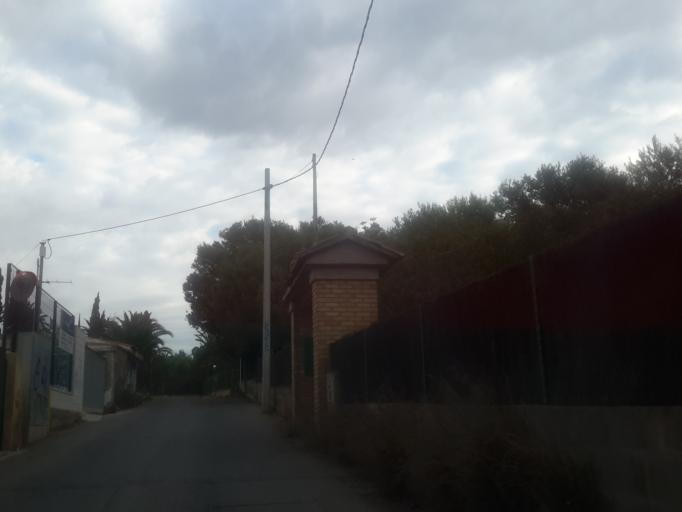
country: ES
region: Catalonia
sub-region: Provincia de Barcelona
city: Cubelles
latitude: 41.2308
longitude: 1.6912
